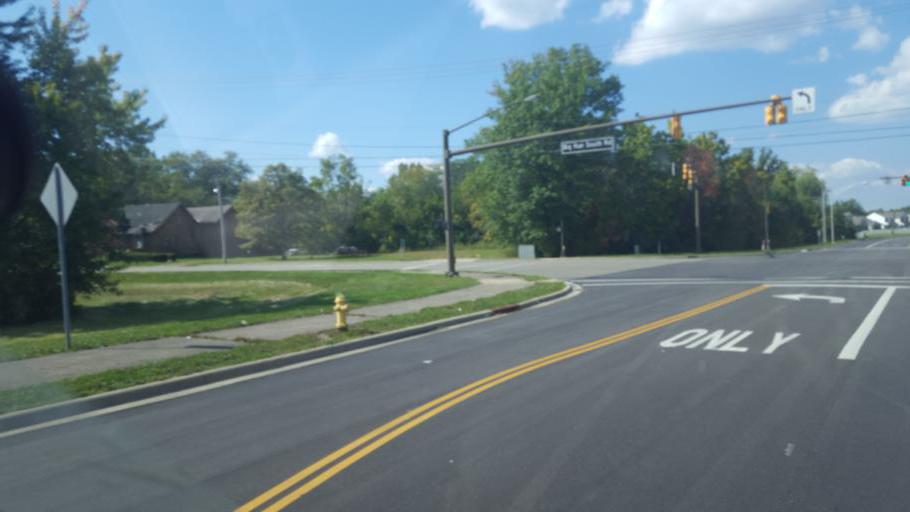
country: US
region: Ohio
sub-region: Franklin County
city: Grove City
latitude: 39.8978
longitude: -83.1071
